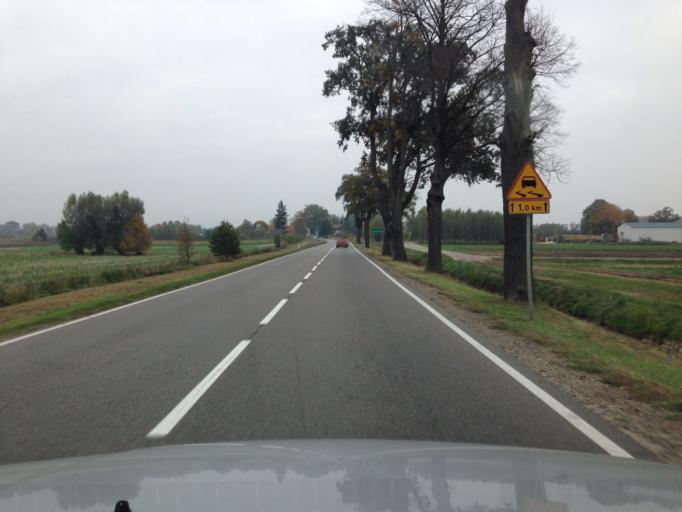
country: PL
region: Warmian-Masurian Voivodeship
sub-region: Powiat elblaski
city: Gronowo Elblaskie
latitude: 54.1267
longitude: 19.3095
